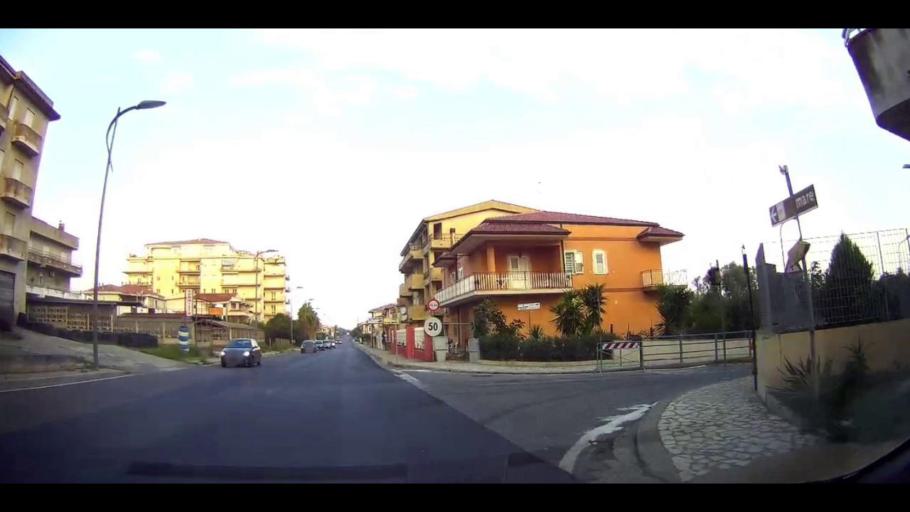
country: IT
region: Calabria
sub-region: Provincia di Crotone
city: Torretta
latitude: 39.4550
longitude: 17.0345
